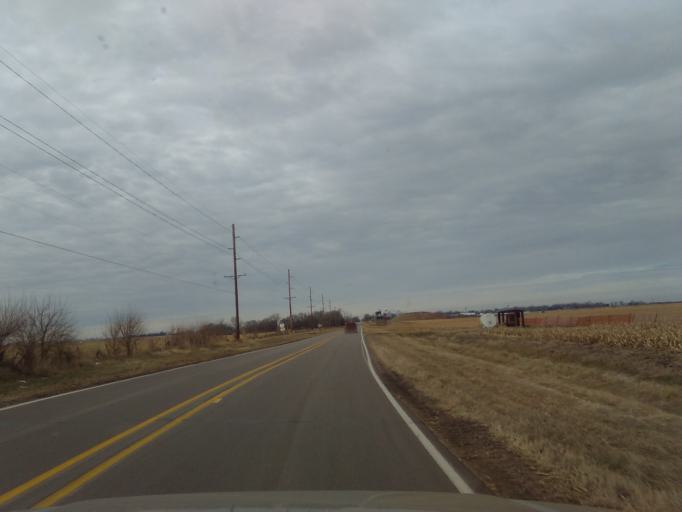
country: US
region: Nebraska
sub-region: Hall County
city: Grand Island
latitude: 40.7710
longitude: -98.3439
